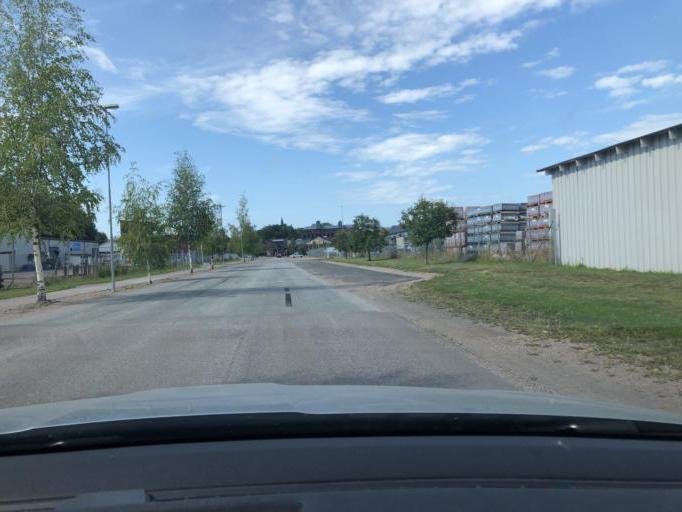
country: SE
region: Dalarna
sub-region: Avesta Kommun
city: Avesta
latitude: 60.1473
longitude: 16.1796
